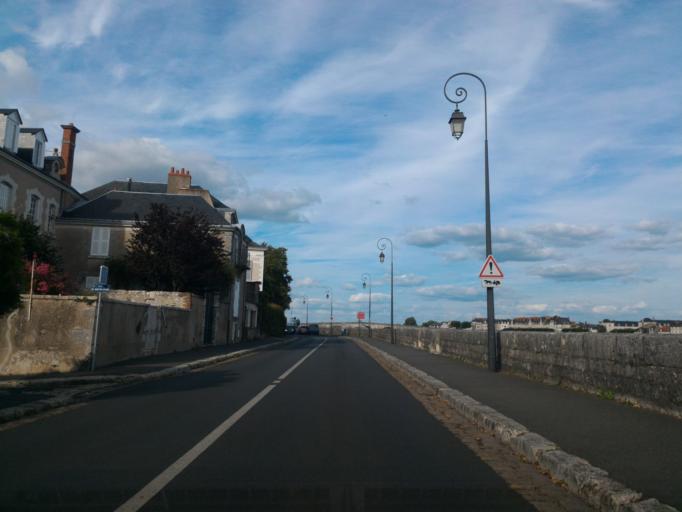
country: FR
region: Centre
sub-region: Departement du Loir-et-Cher
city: Blois
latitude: 47.5819
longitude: 1.3299
